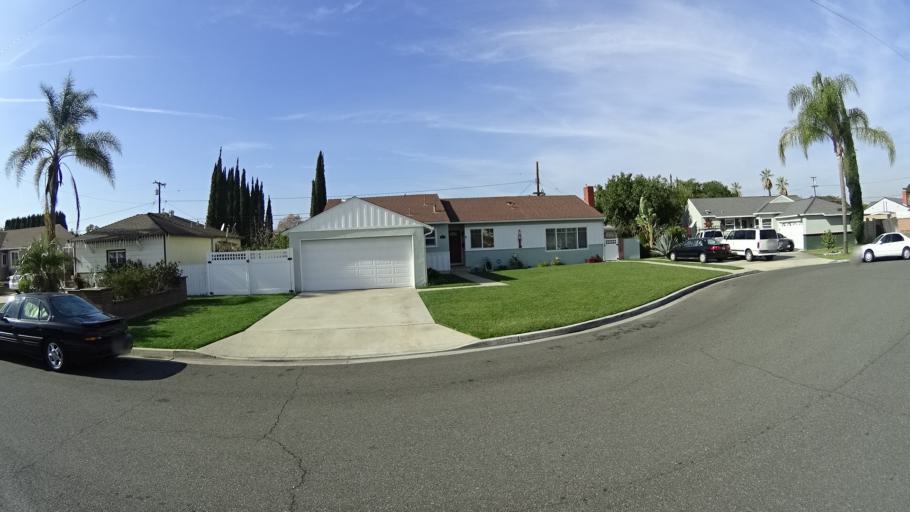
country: US
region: California
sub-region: Orange County
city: Garden Grove
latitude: 33.7976
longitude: -117.9249
